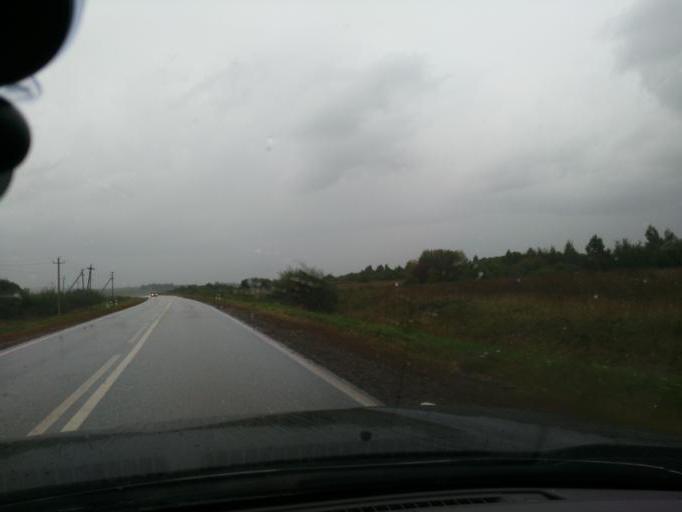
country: RU
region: Perm
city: Barda
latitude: 57.0806
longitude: 55.5427
